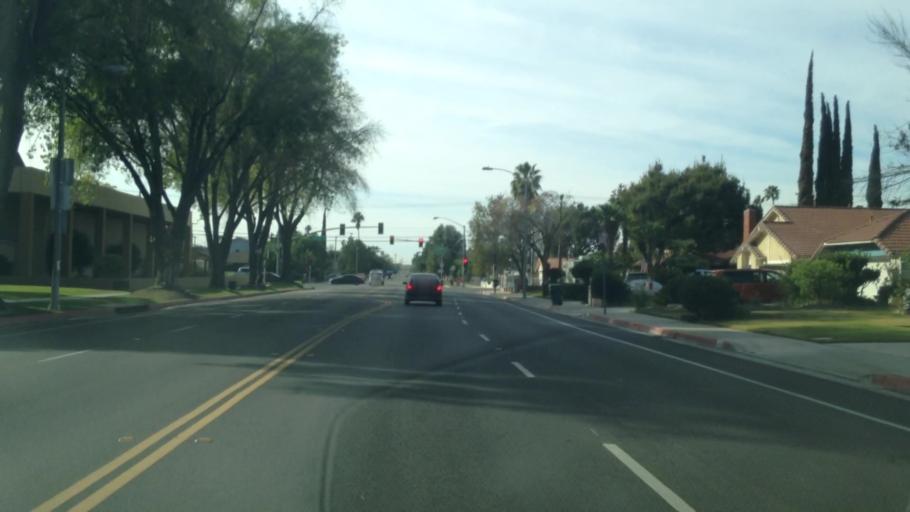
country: US
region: California
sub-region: Riverside County
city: Riverside
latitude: 33.9534
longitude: -117.4173
